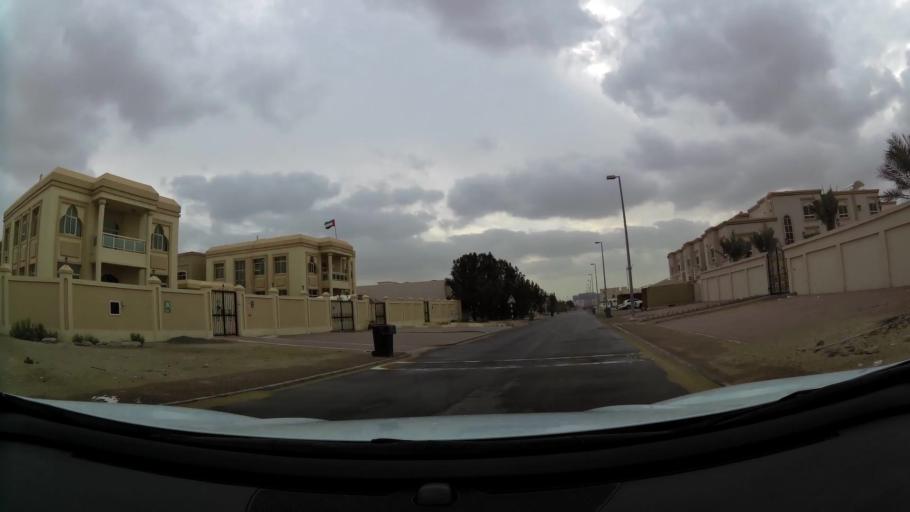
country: AE
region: Abu Dhabi
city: Abu Dhabi
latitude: 24.3487
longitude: 54.6341
